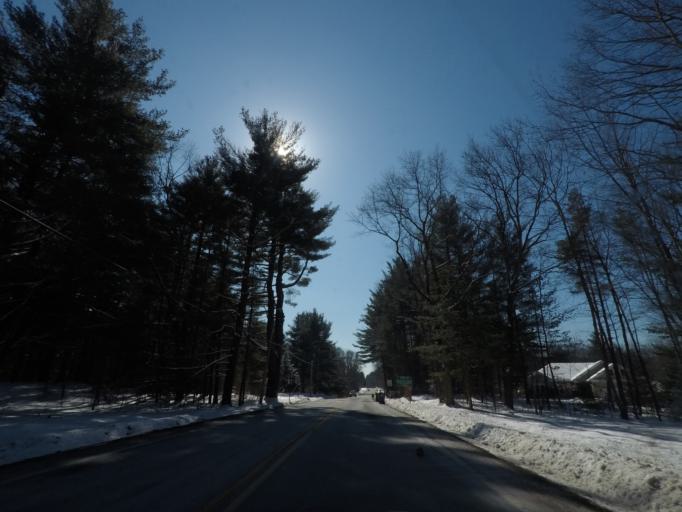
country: US
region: New York
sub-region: Saratoga County
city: Country Knolls
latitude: 42.9233
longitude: -73.8230
